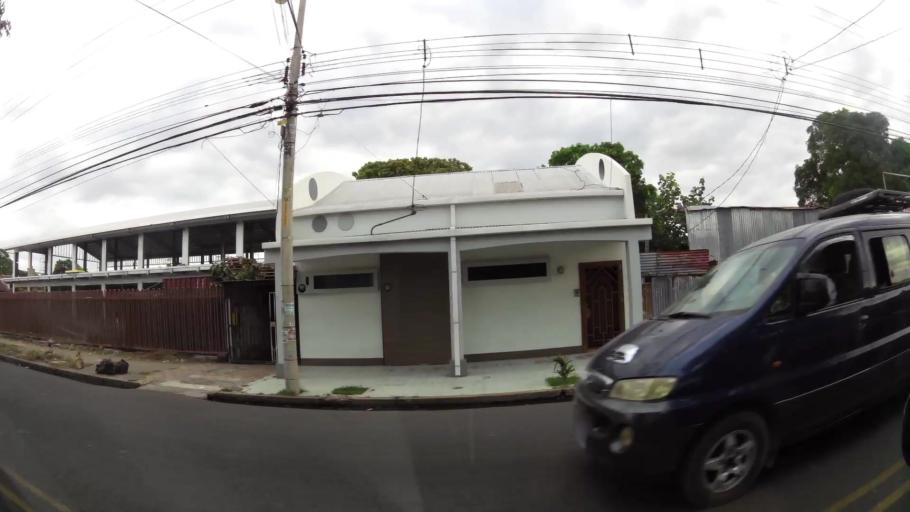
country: CR
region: Puntarenas
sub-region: Canton Central de Puntarenas
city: Puntarenas
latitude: 9.9780
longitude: -84.8283
